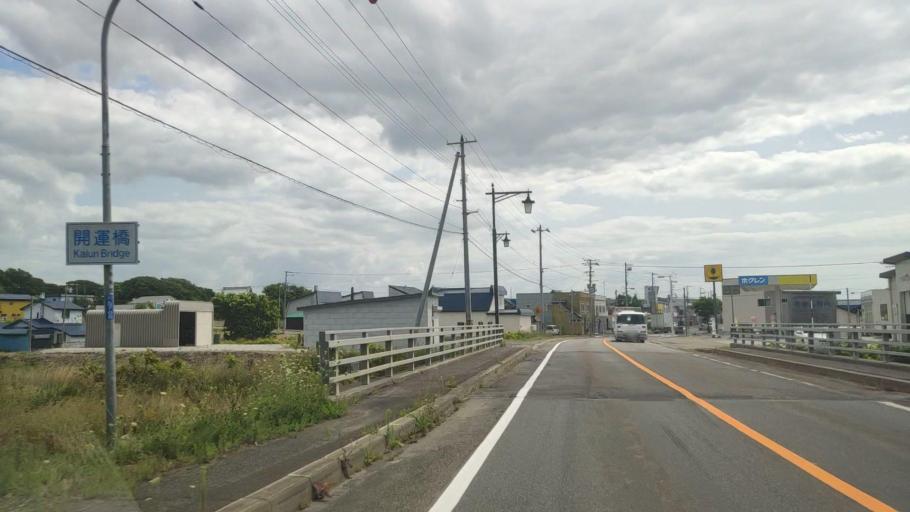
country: JP
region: Hokkaido
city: Rumoi
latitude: 44.5359
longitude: 141.7672
